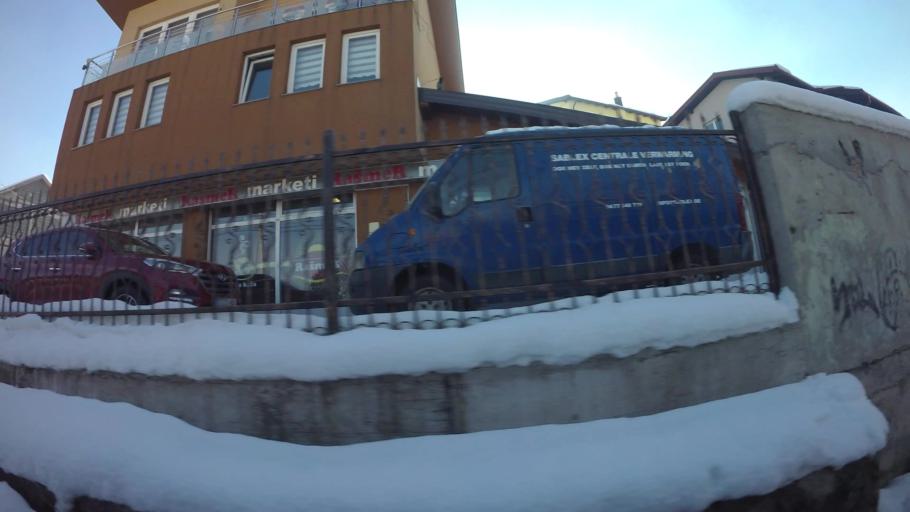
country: BA
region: Federation of Bosnia and Herzegovina
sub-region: Kanton Sarajevo
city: Sarajevo
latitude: 43.8397
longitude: 18.3737
